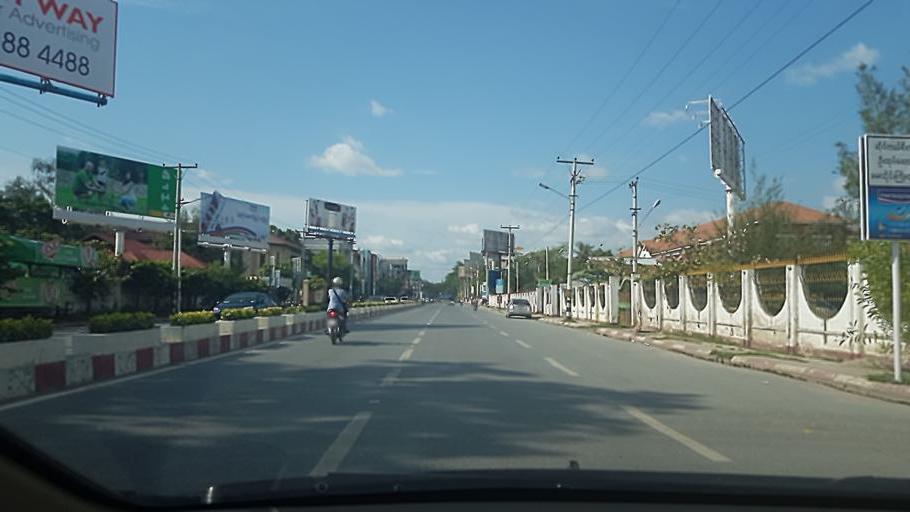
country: MM
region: Mandalay
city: Mandalay
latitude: 21.9785
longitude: 96.0871
